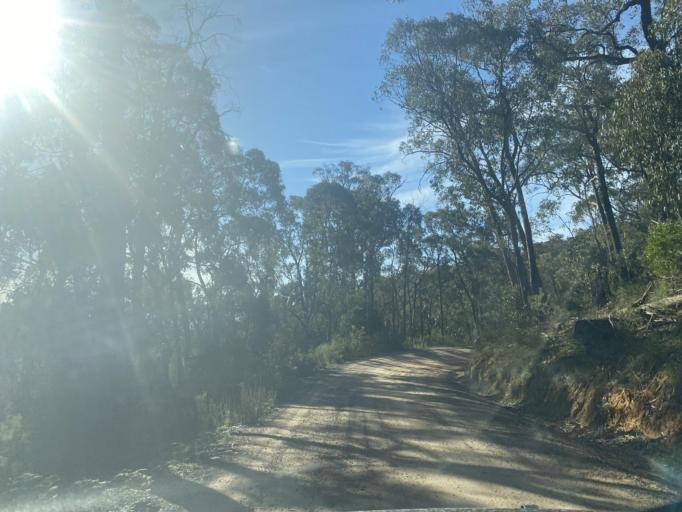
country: AU
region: Victoria
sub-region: Mansfield
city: Mansfield
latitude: -36.8340
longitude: 146.1675
